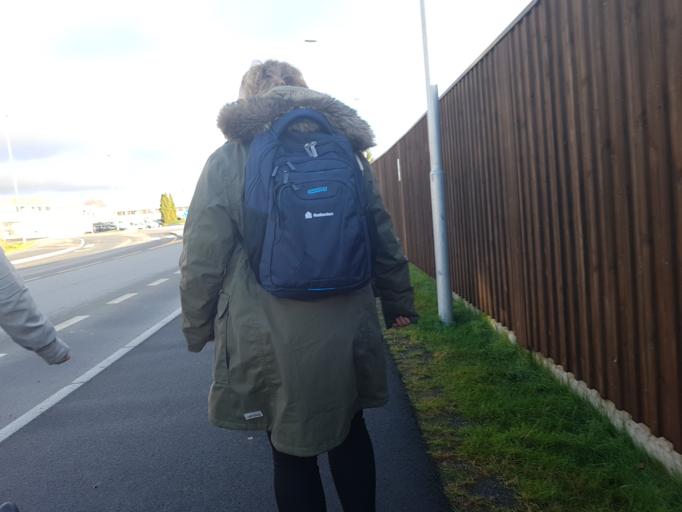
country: NO
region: Akershus
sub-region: Ullensaker
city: Jessheim
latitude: 60.1440
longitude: 11.1824
